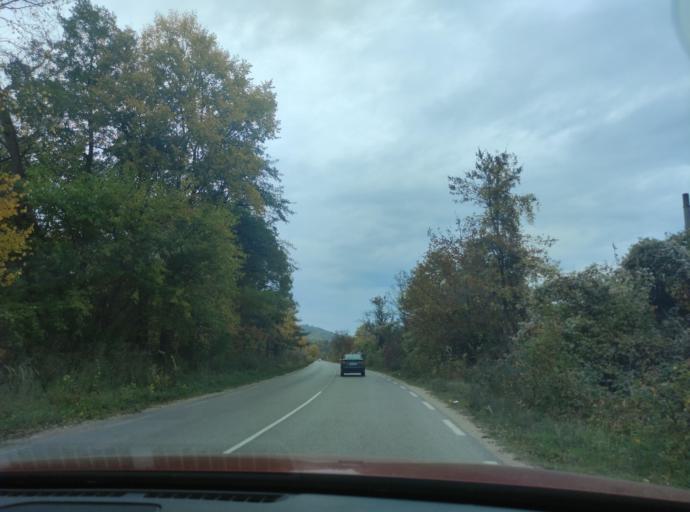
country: BG
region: Montana
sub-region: Obshtina Berkovitsa
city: Berkovitsa
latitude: 43.2675
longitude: 23.1751
